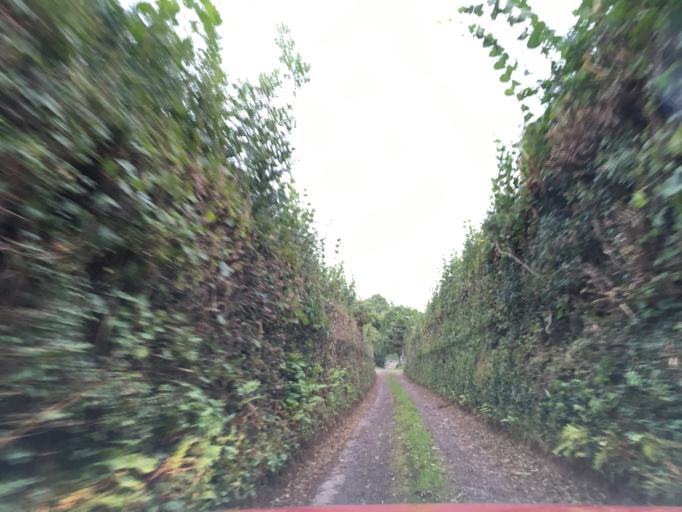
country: GB
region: Wales
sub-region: Monmouthshire
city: Llangybi
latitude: 51.6528
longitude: -2.8735
